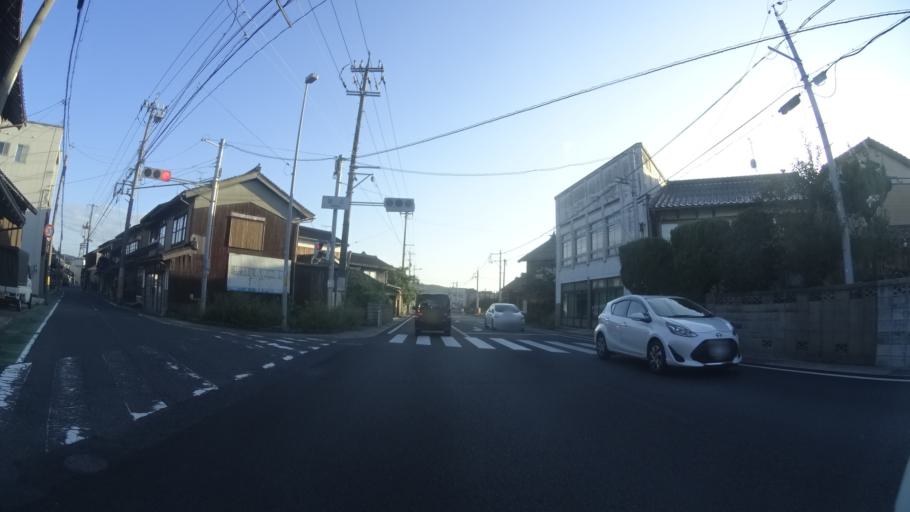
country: JP
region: Tottori
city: Yonago
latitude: 35.4634
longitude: 133.4290
